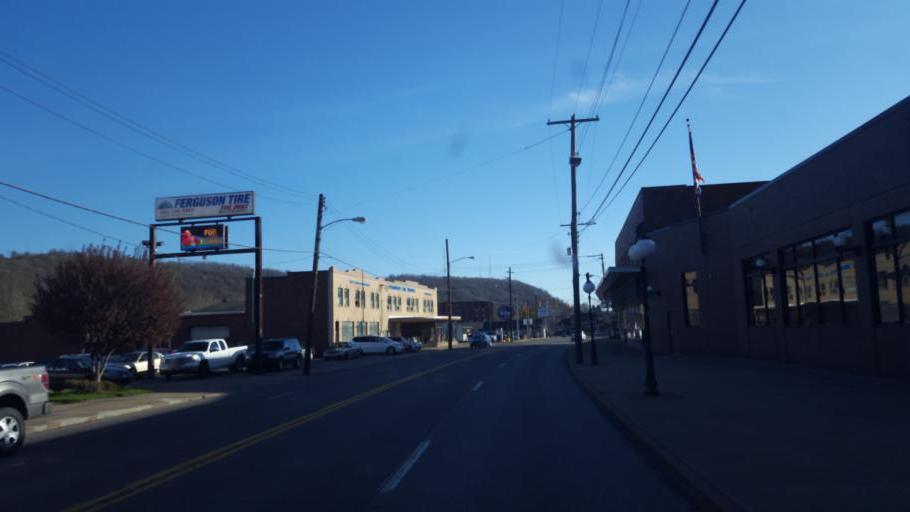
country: US
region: West Virginia
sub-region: Hancock County
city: Weirton
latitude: 40.4004
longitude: -80.5901
